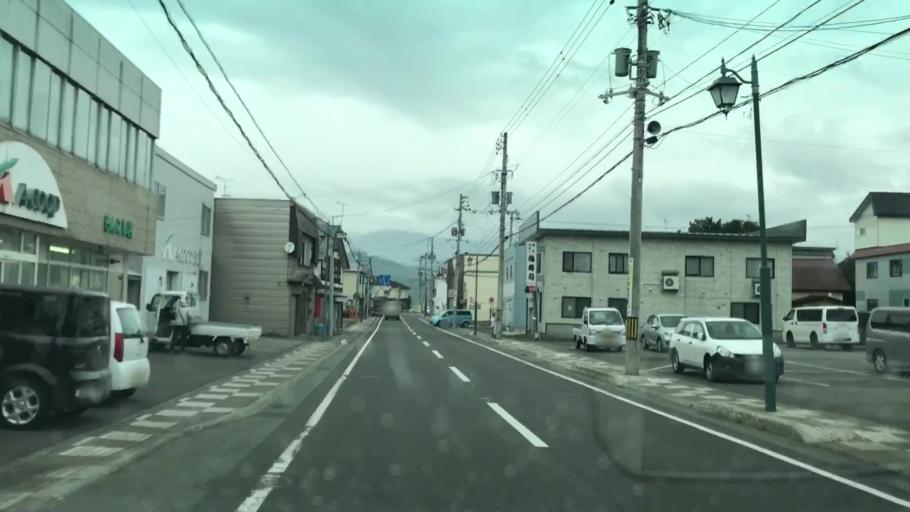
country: JP
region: Hokkaido
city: Niseko Town
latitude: 42.8061
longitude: 140.5288
